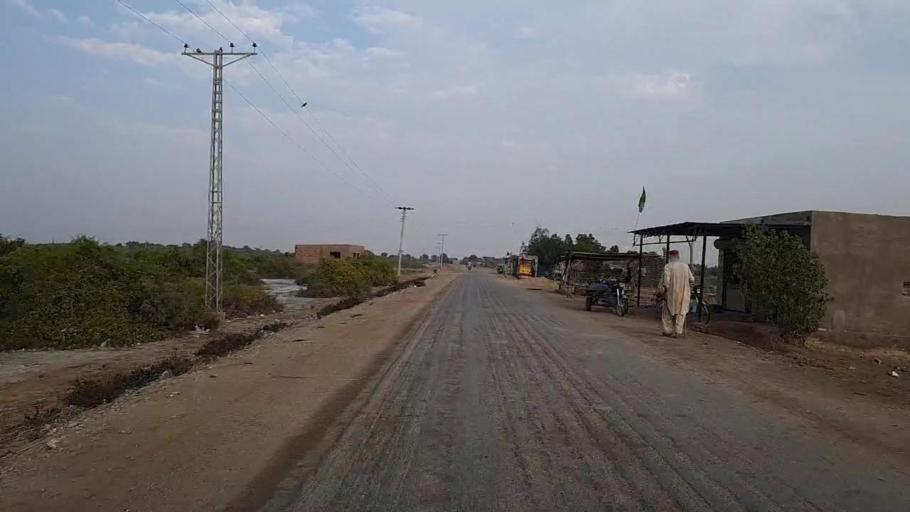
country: PK
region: Sindh
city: Samaro
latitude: 25.3824
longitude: 69.3349
